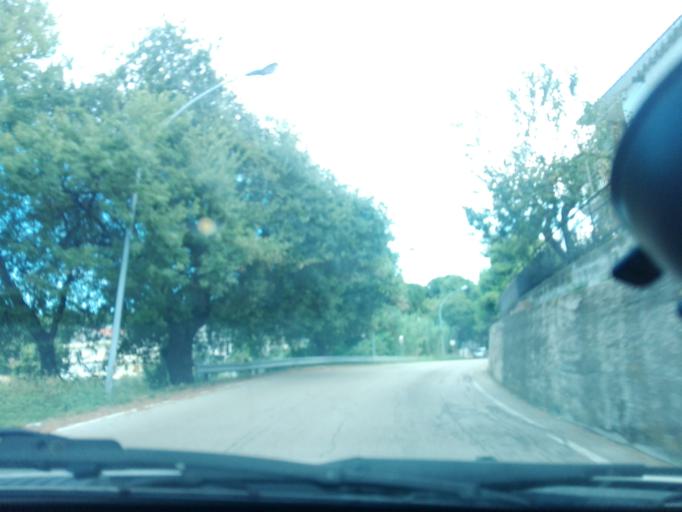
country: IT
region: Abruzzo
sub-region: Provincia di Pescara
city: Montesilvano Marina
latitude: 42.4958
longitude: 14.1435
